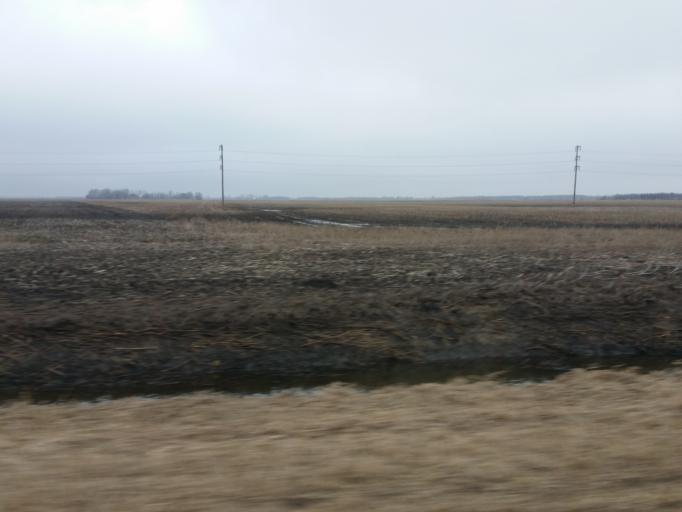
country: US
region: North Dakota
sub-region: Walsh County
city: Grafton
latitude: 48.3531
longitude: -97.1736
